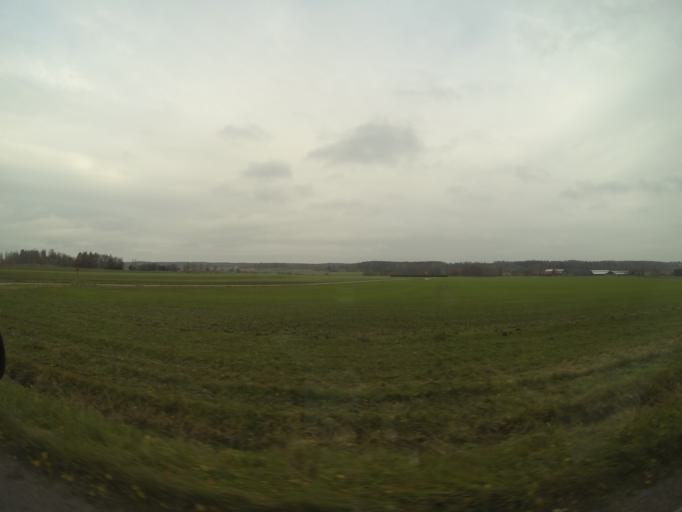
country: SE
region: Vaestmanland
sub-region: Vasteras
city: Skultuna
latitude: 59.6727
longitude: 16.4541
